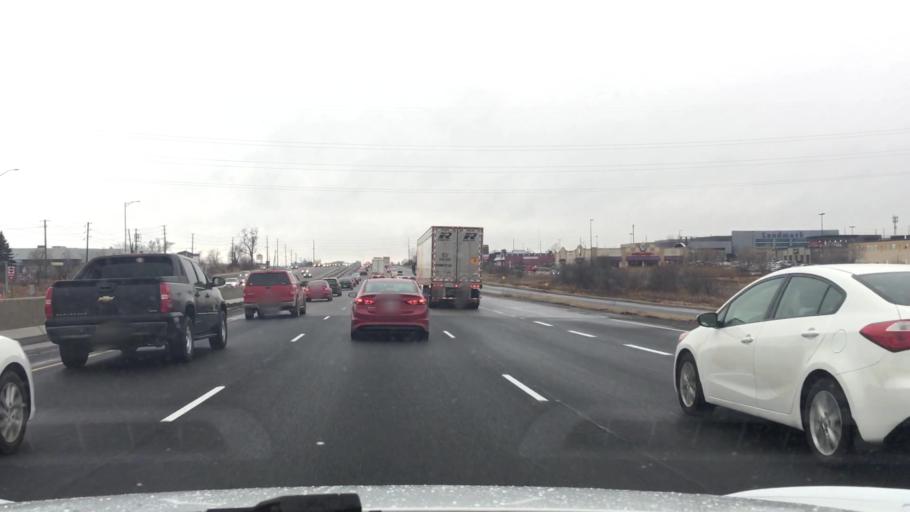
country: CA
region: Ontario
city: Oshawa
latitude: 43.8689
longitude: -78.9080
